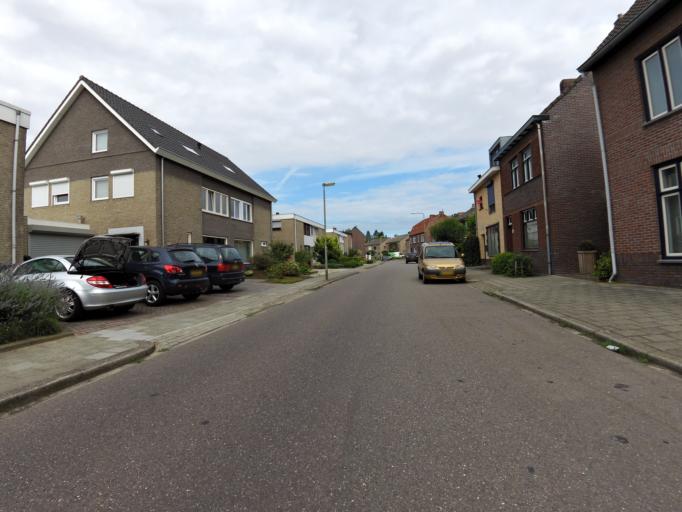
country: NL
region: Limburg
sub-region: Gemeente Schinnen
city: Oirsbeek
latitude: 50.9509
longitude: 5.9058
